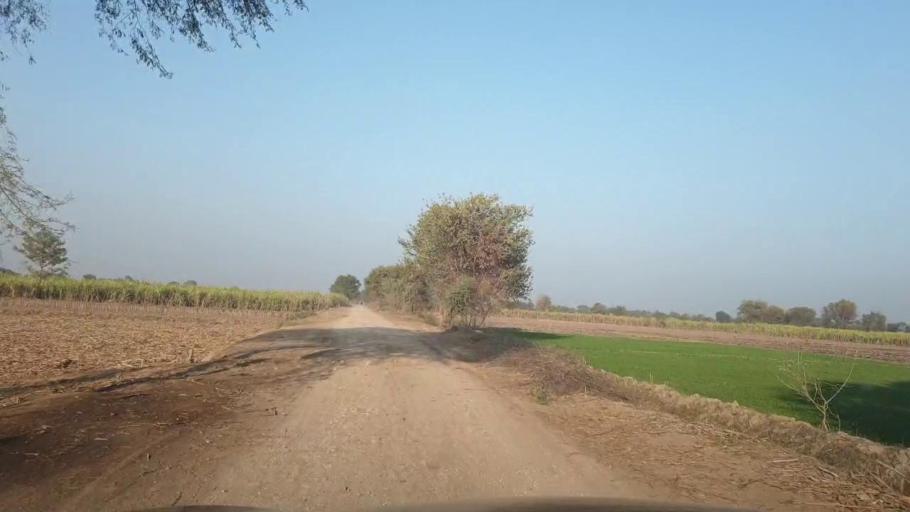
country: PK
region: Sindh
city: Ubauro
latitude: 28.2996
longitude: 69.8024
